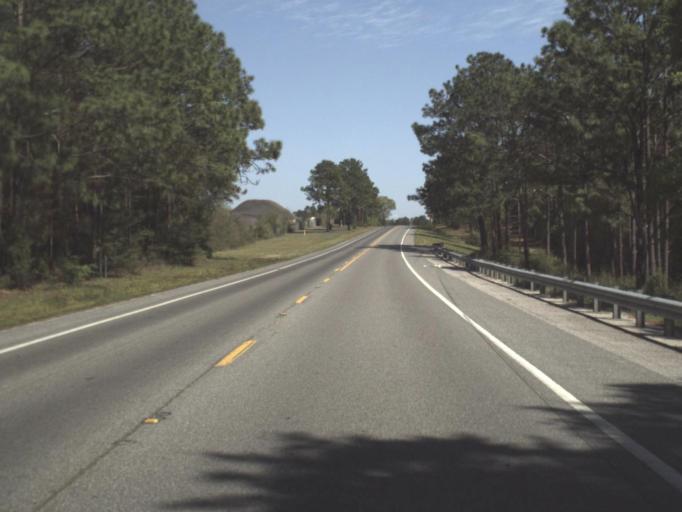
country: US
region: Florida
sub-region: Okaloosa County
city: Crestview
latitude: 30.7237
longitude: -86.6884
